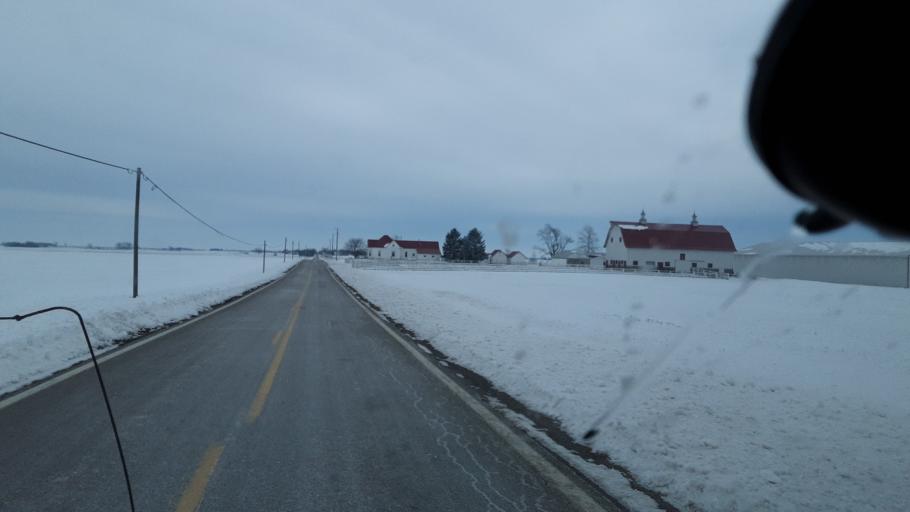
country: US
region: Ohio
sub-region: Madison County
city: Bethel
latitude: 39.7325
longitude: -83.4477
